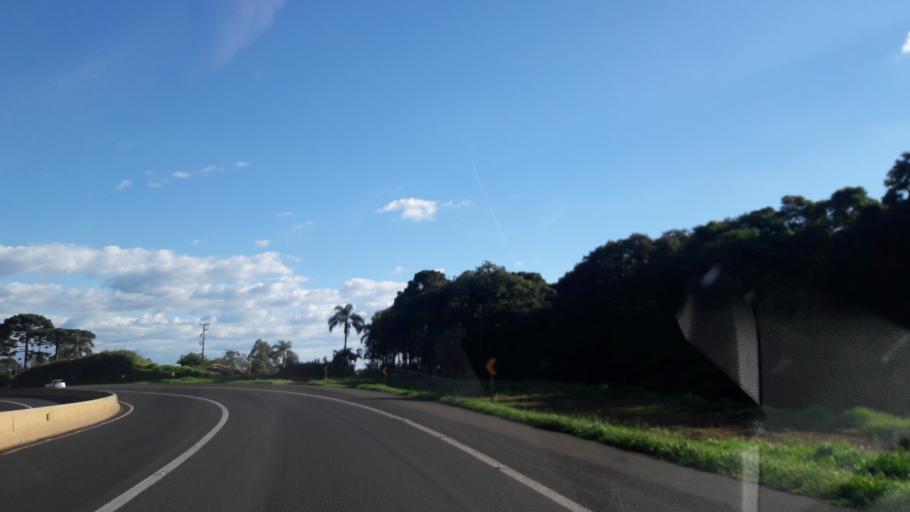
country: BR
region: Parana
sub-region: Guarapuava
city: Guarapuava
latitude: -25.3471
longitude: -51.3915
